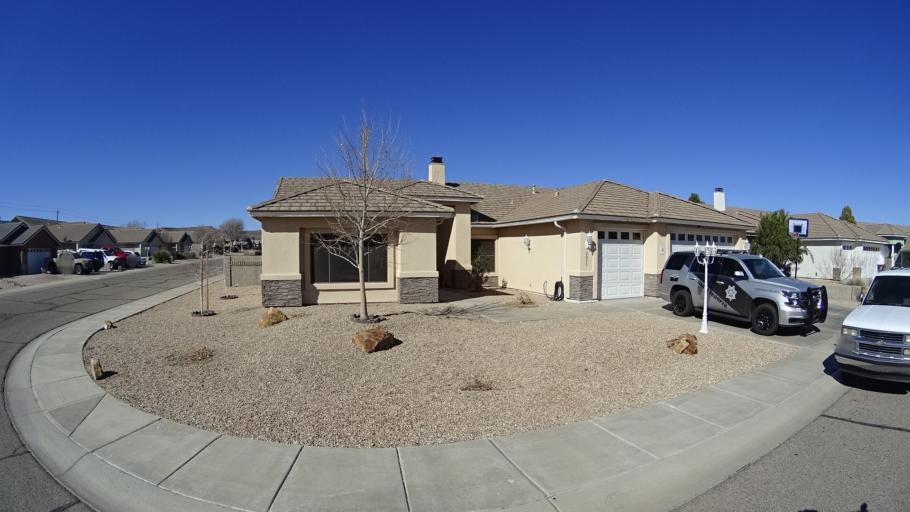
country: US
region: Arizona
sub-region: Mohave County
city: New Kingman-Butler
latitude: 35.2327
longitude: -114.0292
